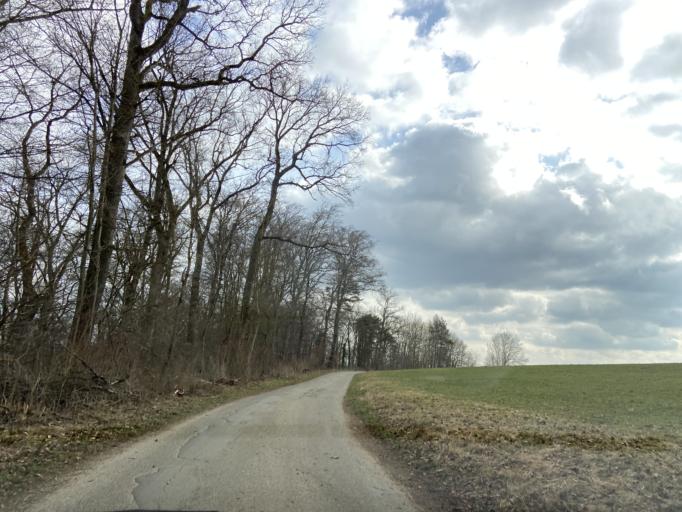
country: DE
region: Baden-Wuerttemberg
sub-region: Tuebingen Region
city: Bingen
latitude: 48.1173
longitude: 9.2590
